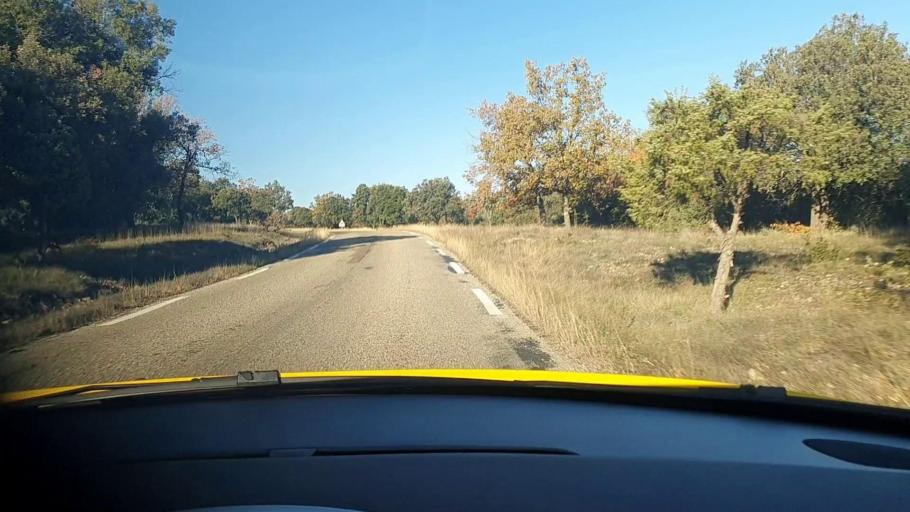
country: FR
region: Languedoc-Roussillon
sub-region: Departement du Gard
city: Barjac
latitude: 44.1666
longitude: 4.3287
